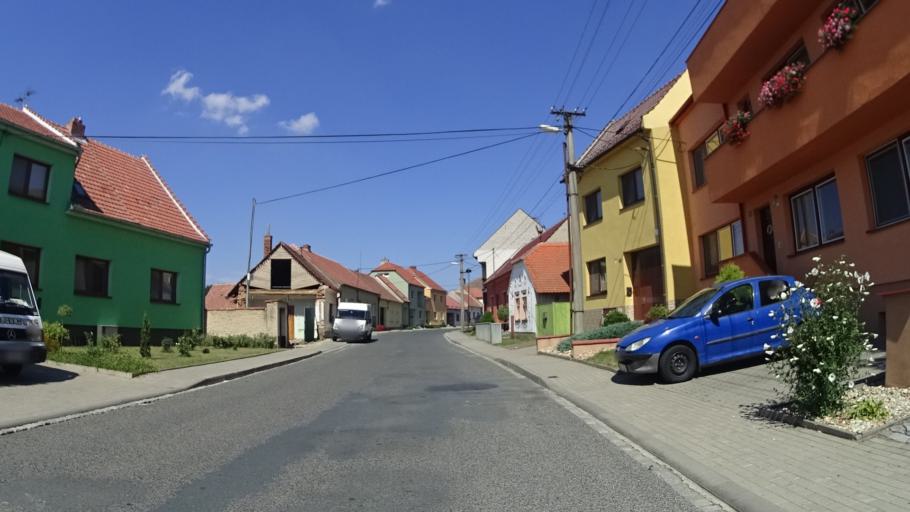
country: CZ
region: South Moravian
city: Vnorovy
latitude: 48.9256
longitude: 17.3433
